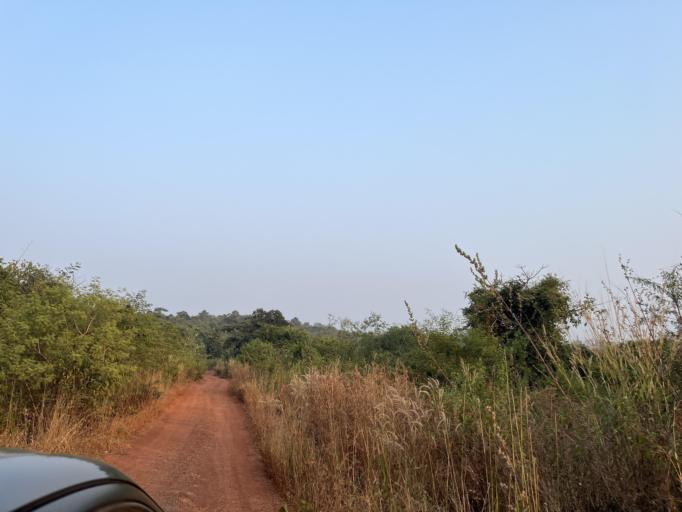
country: IN
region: Goa
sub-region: North Goa
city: Pernem
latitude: 15.7016
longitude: 73.8305
